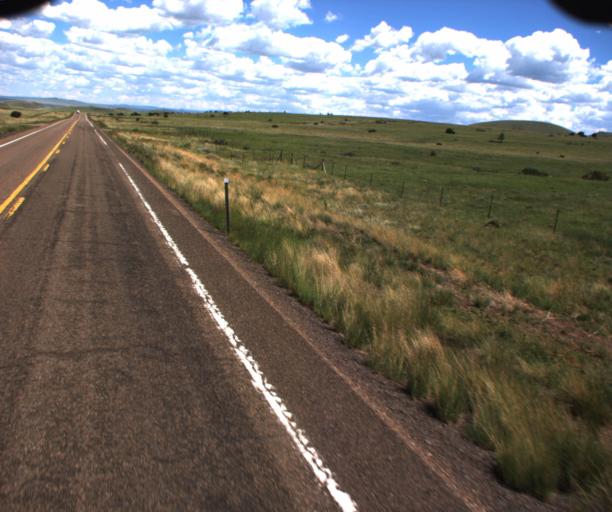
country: US
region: Arizona
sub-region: Apache County
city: Springerville
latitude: 34.2196
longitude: -109.4774
